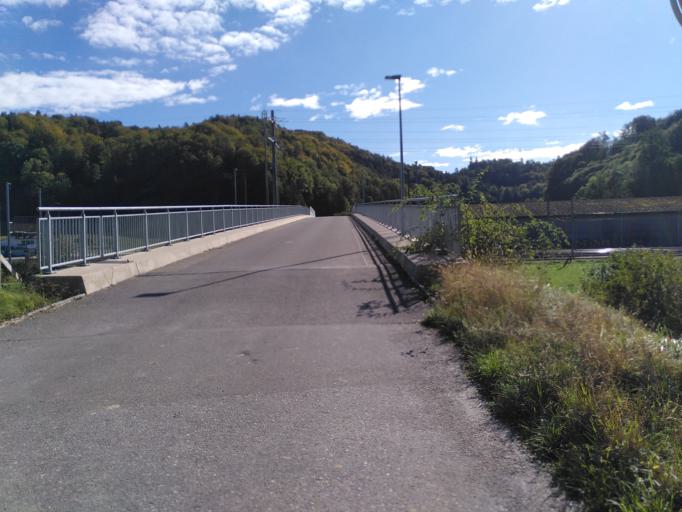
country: CH
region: Bern
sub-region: Oberaargau
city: Seeberg
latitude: 47.1432
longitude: 7.6947
